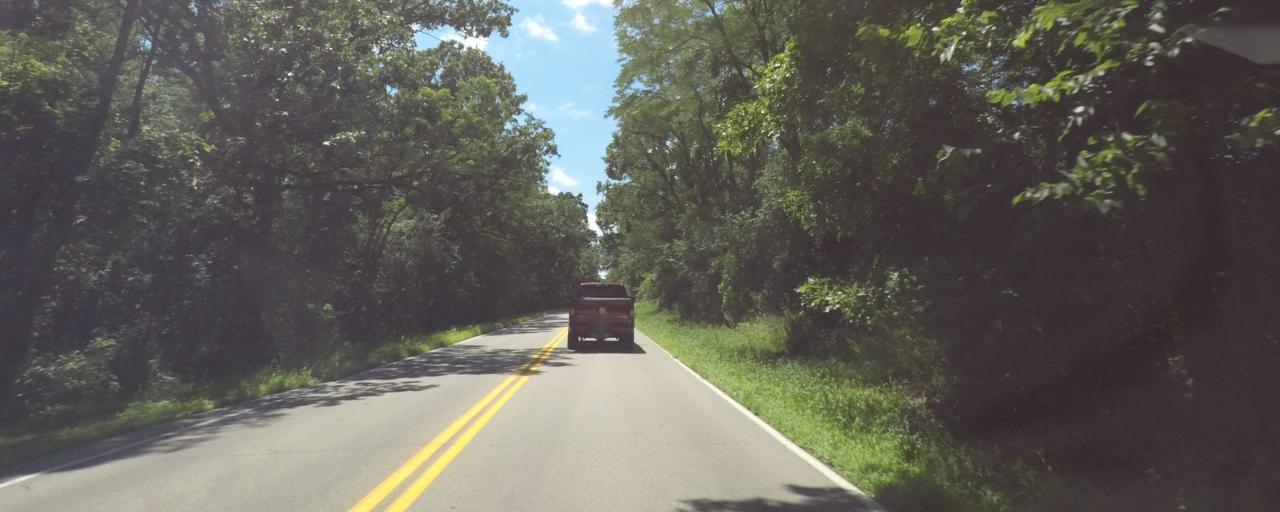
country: US
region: Wisconsin
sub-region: Waukesha County
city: Eagle
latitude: 42.9289
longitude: -88.5143
